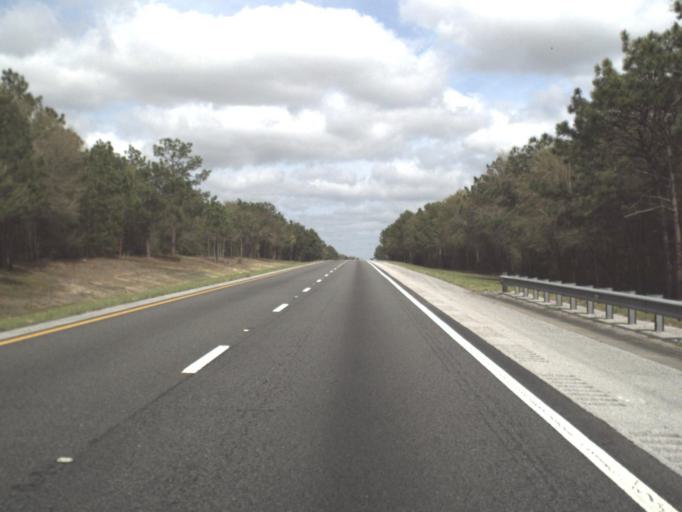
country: US
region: Florida
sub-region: Okaloosa County
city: Crestview
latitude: 30.7313
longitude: -86.3814
